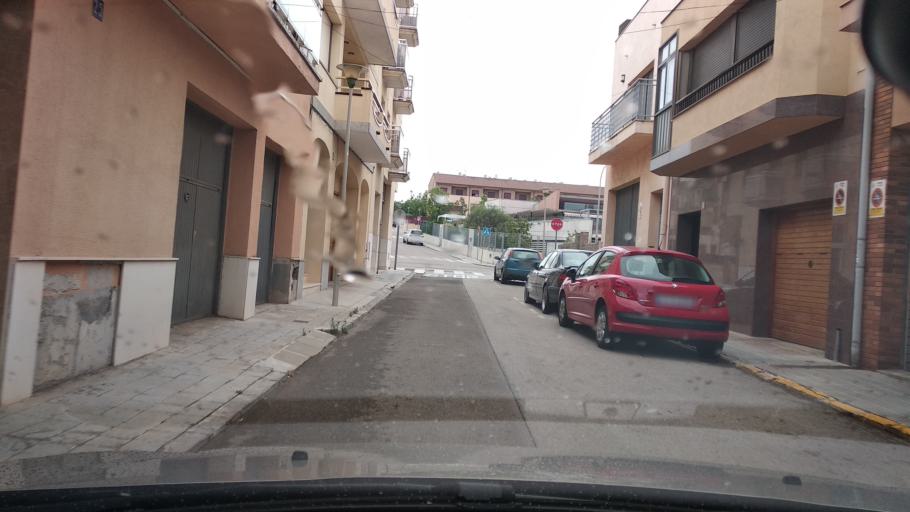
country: ES
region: Catalonia
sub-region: Provincia de Tarragona
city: El Vendrell
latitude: 41.2159
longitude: 1.5269
